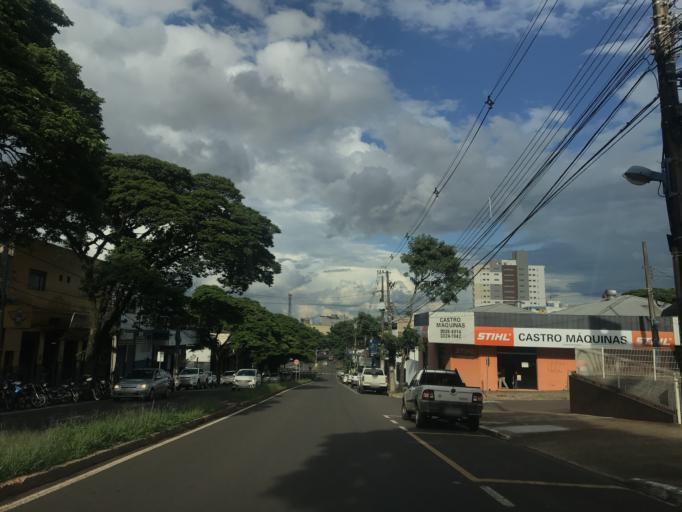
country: BR
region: Parana
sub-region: Maringa
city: Maringa
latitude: -23.4253
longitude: -51.9614
